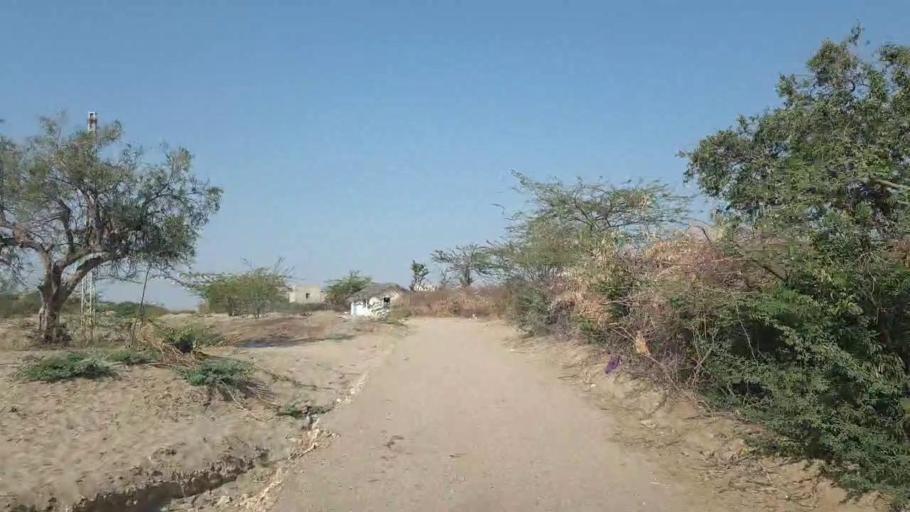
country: PK
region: Sindh
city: Dhoro Naro
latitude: 25.5047
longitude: 69.6030
